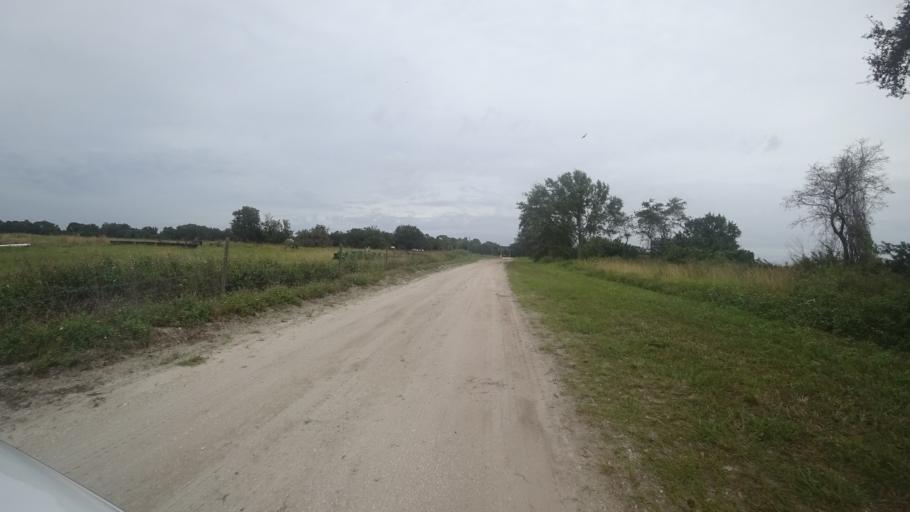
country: US
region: Florida
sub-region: Hillsborough County
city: Wimauma
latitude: 27.5945
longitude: -82.2862
